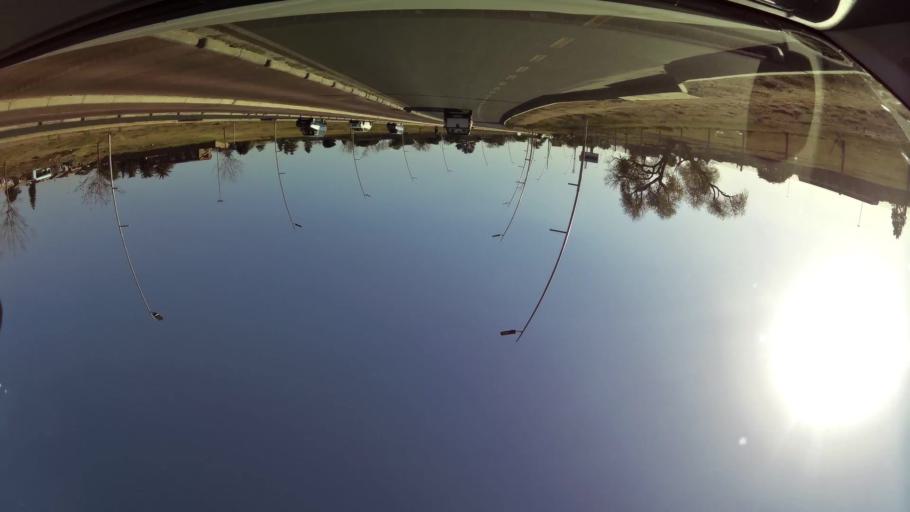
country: ZA
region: Gauteng
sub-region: Ekurhuleni Metropolitan Municipality
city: Tembisa
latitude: -26.0144
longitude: 28.2188
